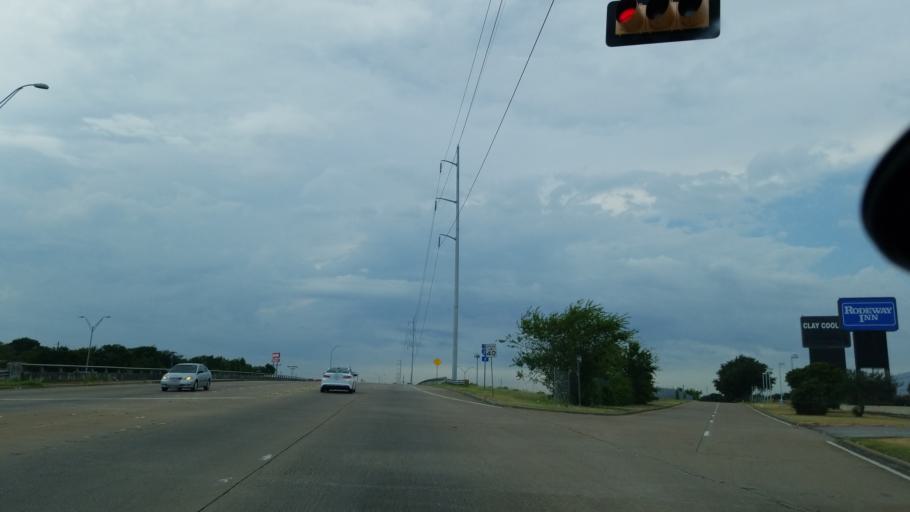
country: US
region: Texas
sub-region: Dallas County
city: Duncanville
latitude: 32.6620
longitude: -96.8937
